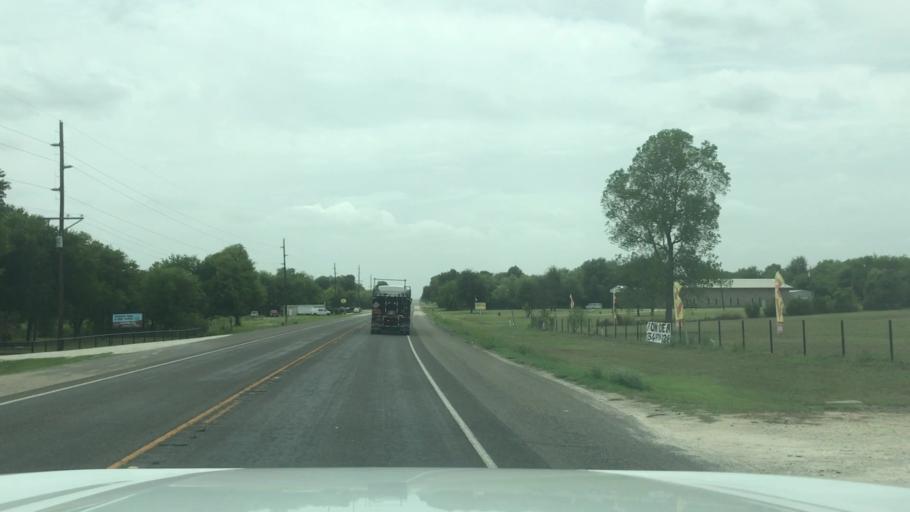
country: US
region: Texas
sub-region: Bosque County
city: Clifton
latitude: 31.7447
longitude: -97.5533
